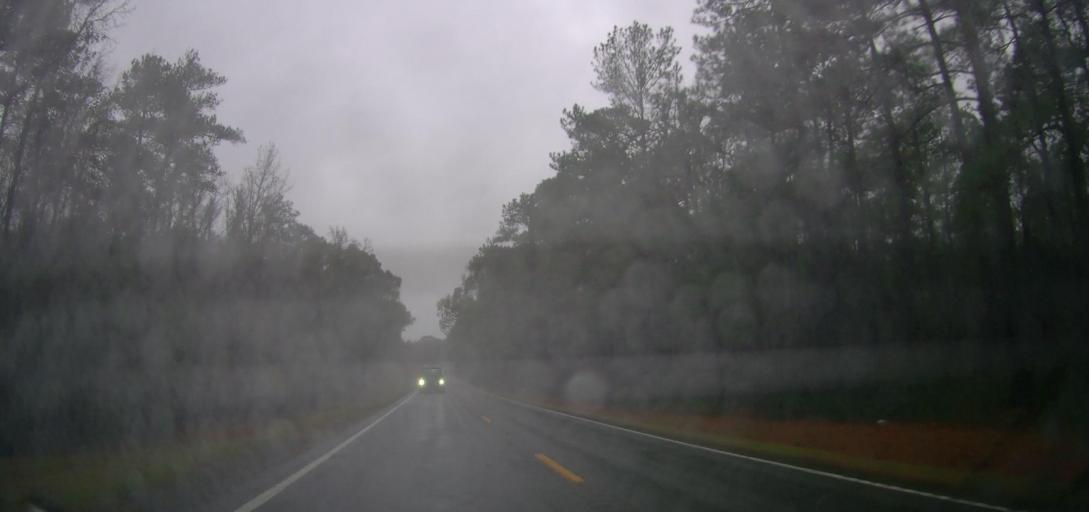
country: US
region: Georgia
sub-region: Jones County
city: Gray
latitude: 33.1407
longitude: -83.4648
